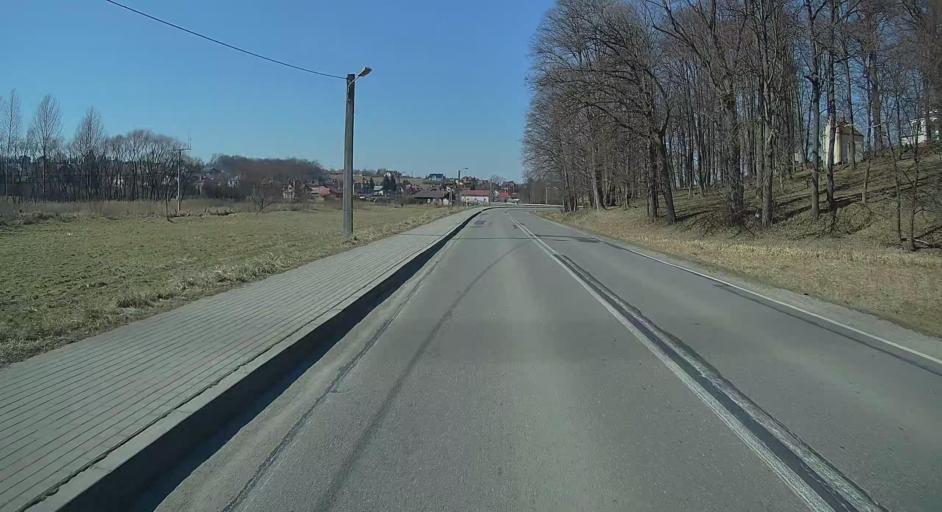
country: PL
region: Subcarpathian Voivodeship
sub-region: Powiat rzeszowski
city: Hyzne
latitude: 49.9221
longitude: 22.1683
